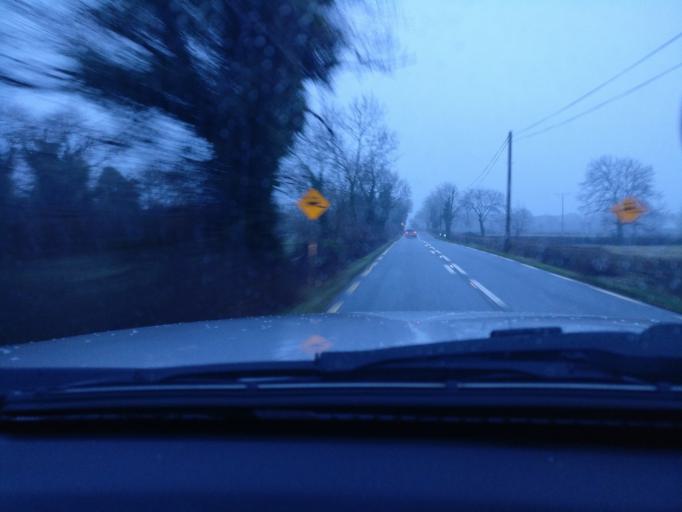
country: IE
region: Leinster
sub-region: An Mhi
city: Athboy
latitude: 53.6393
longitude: -6.8319
